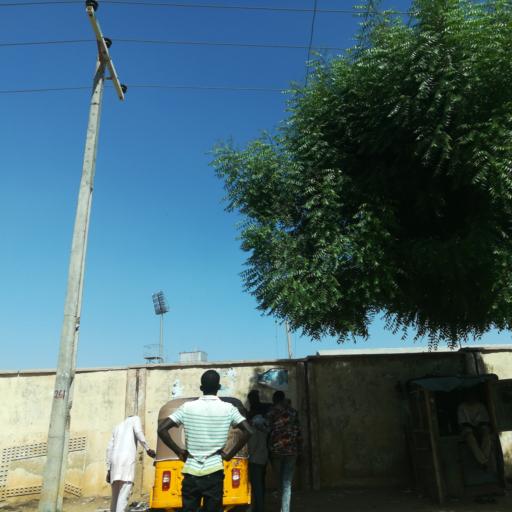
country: NG
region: Kano
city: Kano
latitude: 11.9982
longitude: 8.5291
